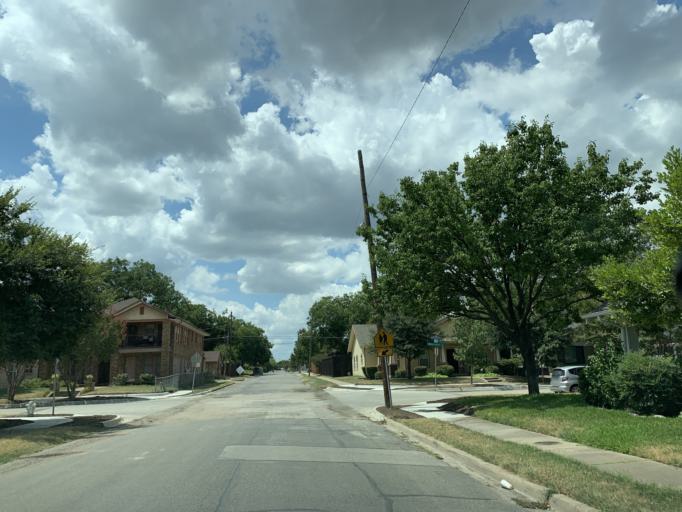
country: US
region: Texas
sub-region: Dallas County
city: Cockrell Hill
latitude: 32.7509
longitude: -96.8449
